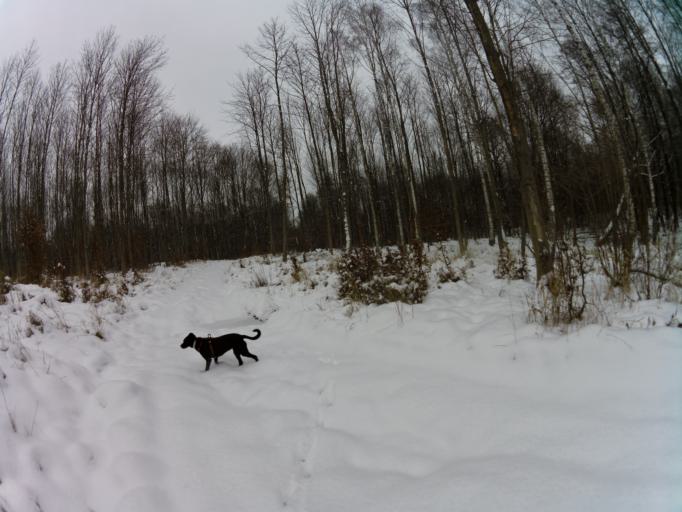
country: PL
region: West Pomeranian Voivodeship
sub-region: Powiat choszczenski
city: Recz
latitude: 53.3280
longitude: 15.5449
